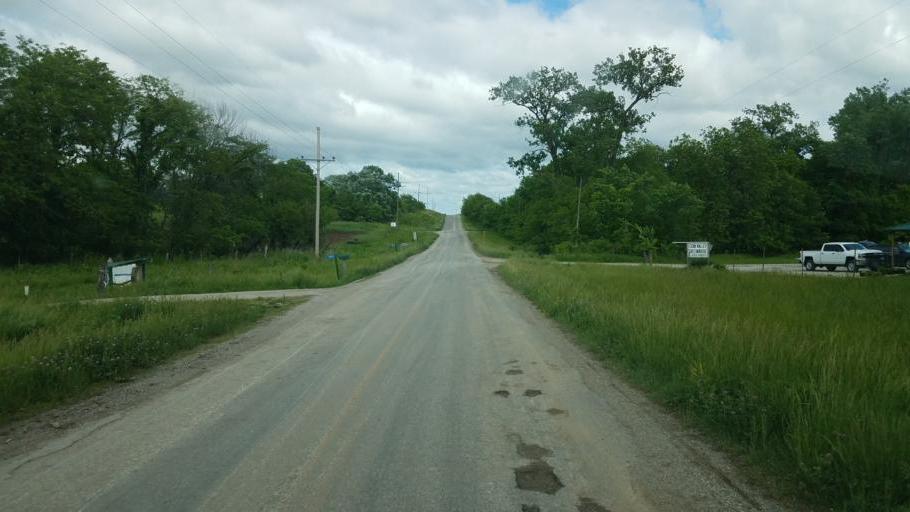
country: US
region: Missouri
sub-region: Mercer County
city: Princeton
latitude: 40.3002
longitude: -93.7113
